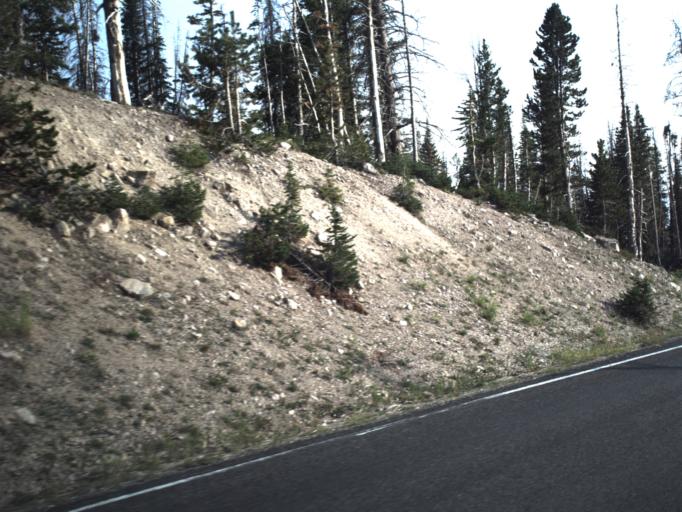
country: US
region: Utah
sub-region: Summit County
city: Kamas
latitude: 40.7218
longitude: -110.8657
